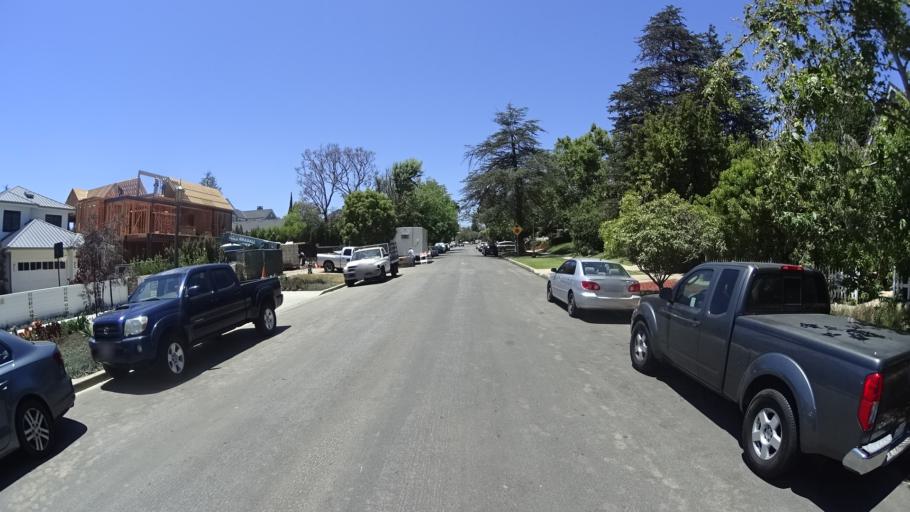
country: US
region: California
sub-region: Los Angeles County
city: Santa Monica
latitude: 34.0441
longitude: -118.4850
